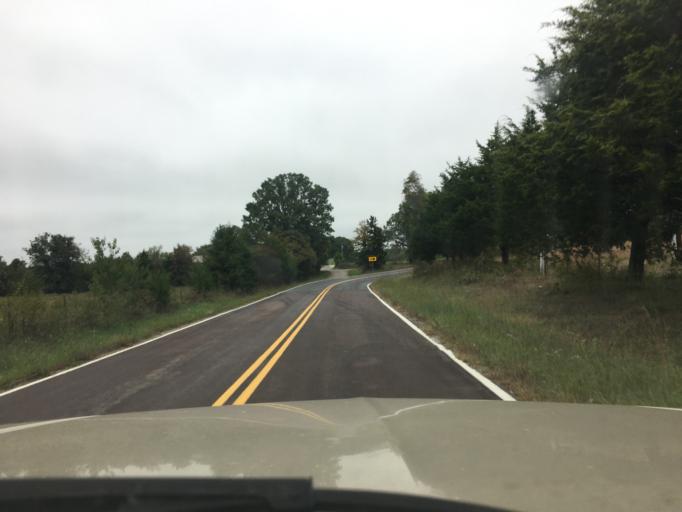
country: US
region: Missouri
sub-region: Crawford County
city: Cuba
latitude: 38.1873
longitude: -91.4849
